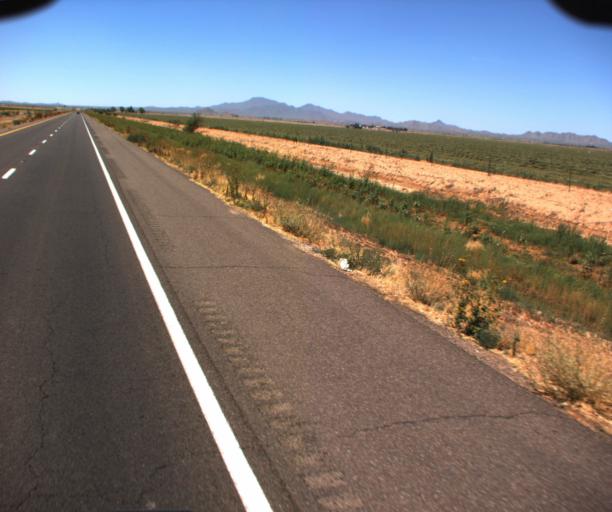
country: US
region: Arizona
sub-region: Pinal County
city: Maricopa
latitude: 32.9555
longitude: -112.0480
